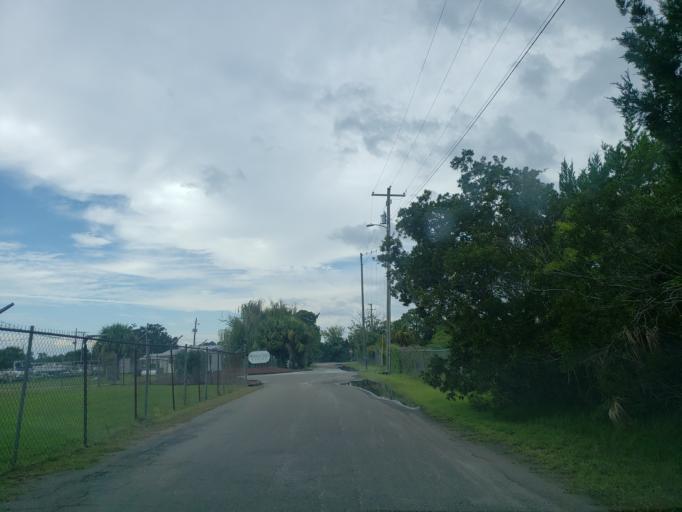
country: US
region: Georgia
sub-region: Chatham County
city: Thunderbolt
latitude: 32.0351
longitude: -81.0436
